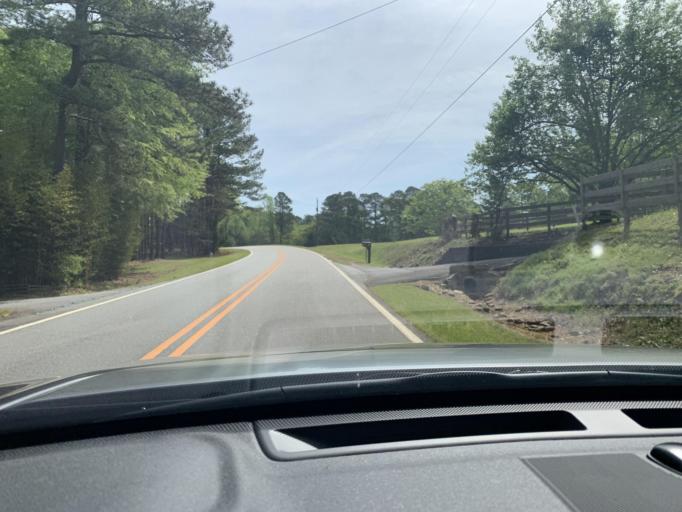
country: US
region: Georgia
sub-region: Oconee County
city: Watkinsville
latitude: 33.8446
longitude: -83.4726
